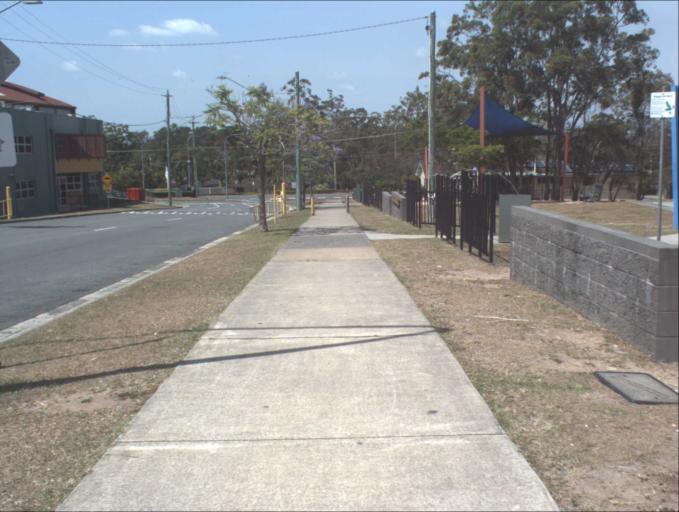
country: AU
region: Queensland
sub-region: Logan
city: Slacks Creek
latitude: -27.6651
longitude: 153.1871
